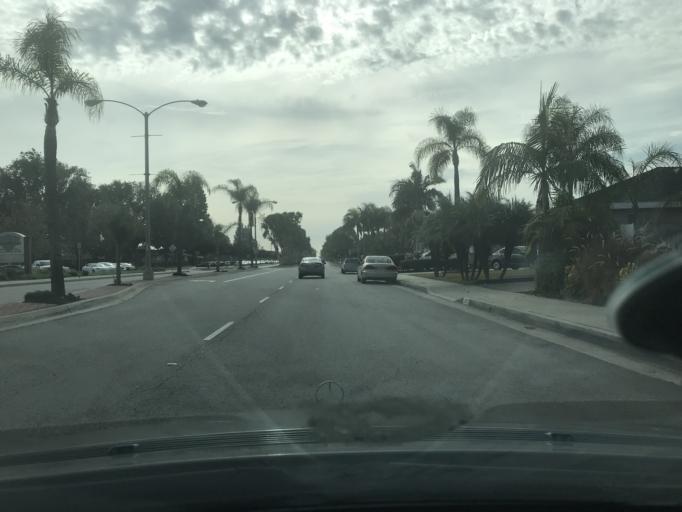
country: US
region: California
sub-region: Los Angeles County
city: Santa Fe Springs
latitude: 33.9427
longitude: -118.0907
